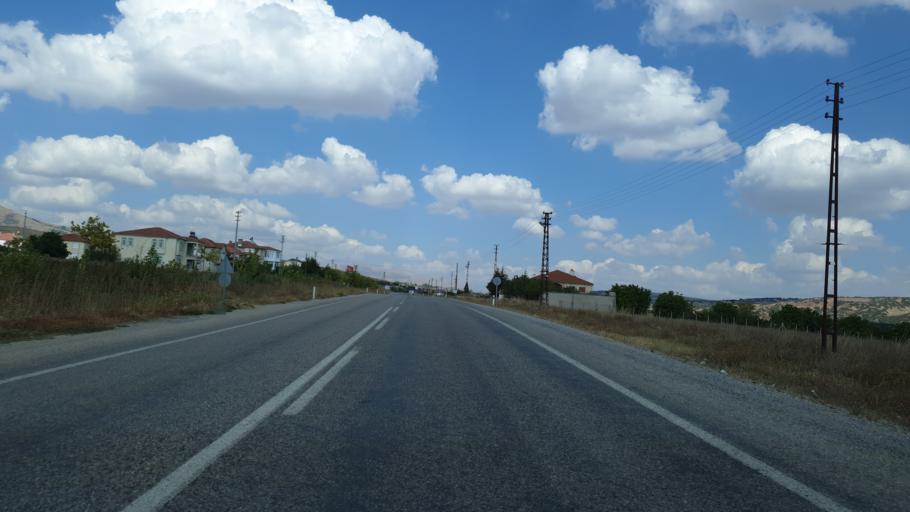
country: TR
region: Kayseri
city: Felahiye
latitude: 39.0968
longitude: 35.5814
